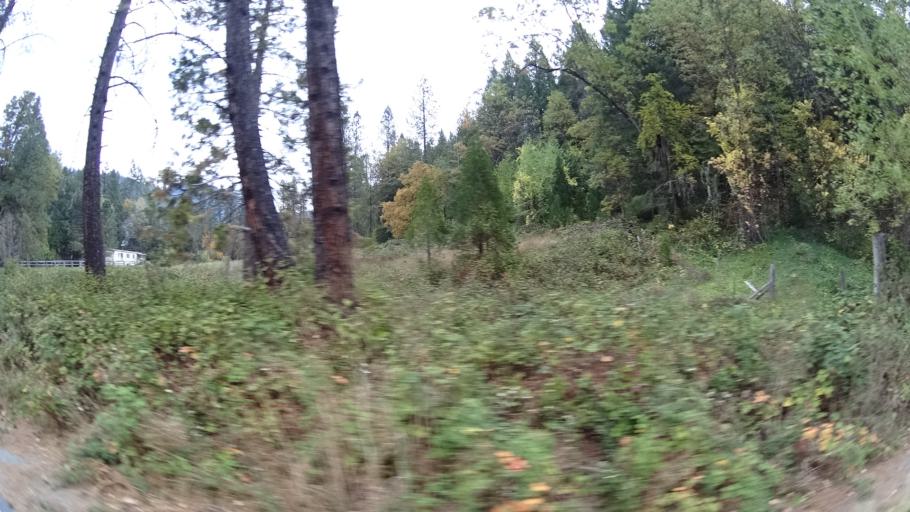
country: US
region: California
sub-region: Siskiyou County
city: Happy Camp
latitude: 41.8775
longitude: -123.4186
